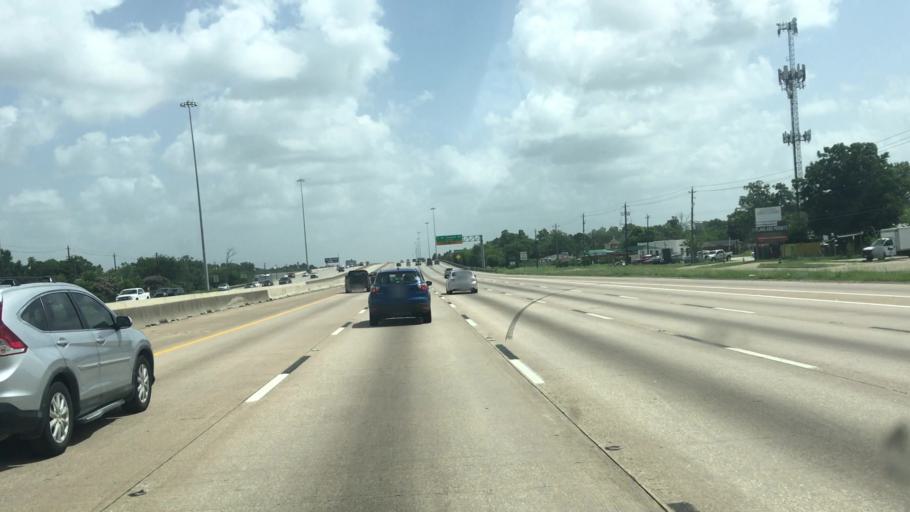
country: US
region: Texas
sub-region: Harris County
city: Aldine
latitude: 29.8748
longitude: -95.3273
